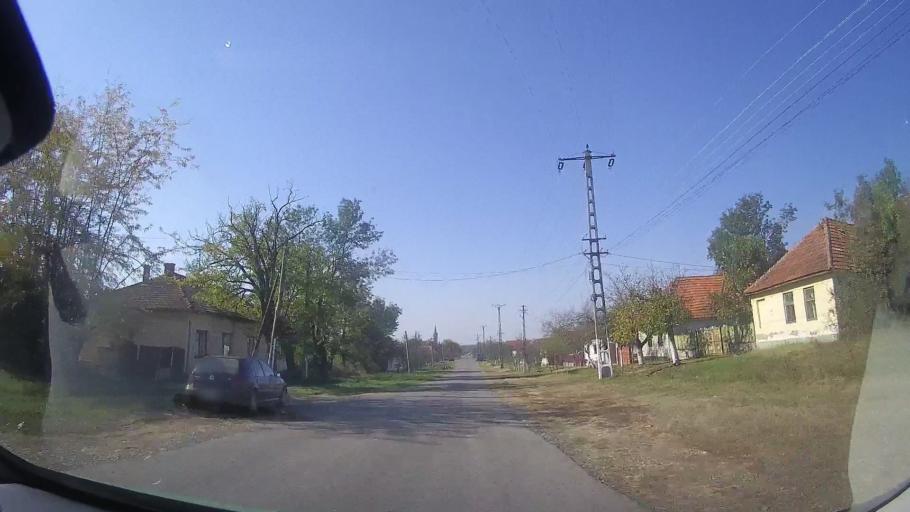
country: RO
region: Timis
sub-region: Comuna Ghizela
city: Ghizela
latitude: 45.8240
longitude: 21.7501
